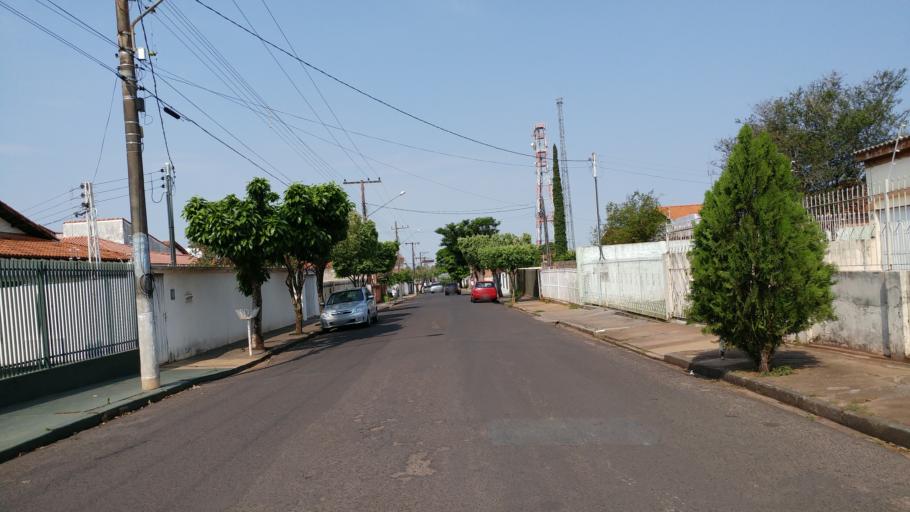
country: BR
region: Sao Paulo
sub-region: Paraguacu Paulista
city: Paraguacu Paulista
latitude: -22.4145
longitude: -50.5809
